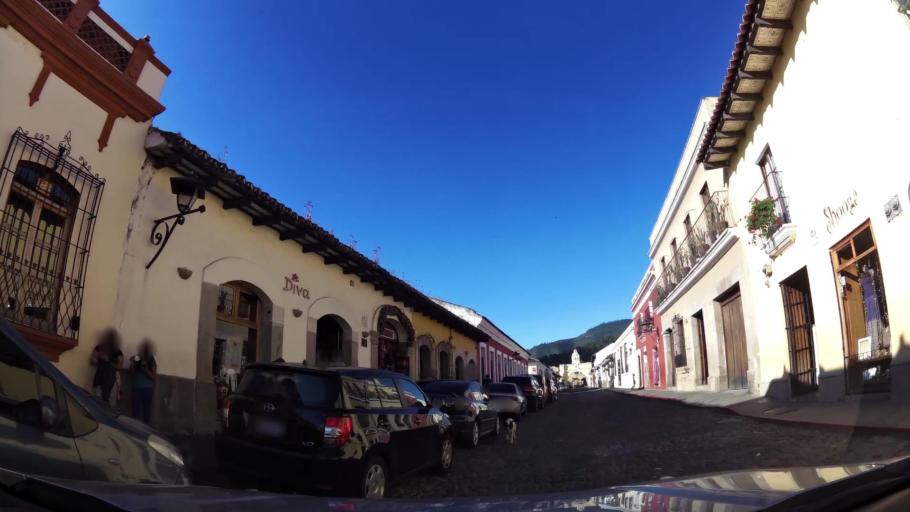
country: GT
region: Sacatepequez
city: Antigua Guatemala
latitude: 14.5577
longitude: -90.7343
